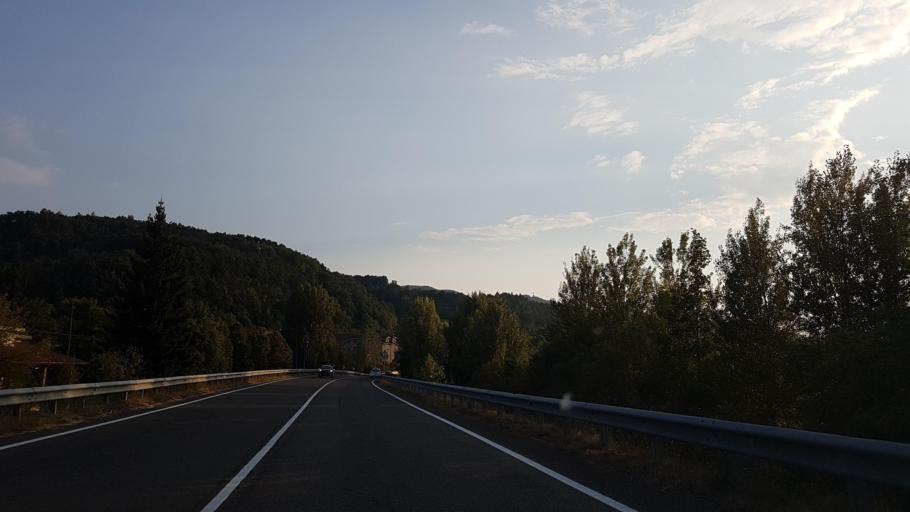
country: IT
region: Emilia-Romagna
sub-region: Provincia di Parma
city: Borgo Val di Taro
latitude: 44.4883
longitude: 9.7725
